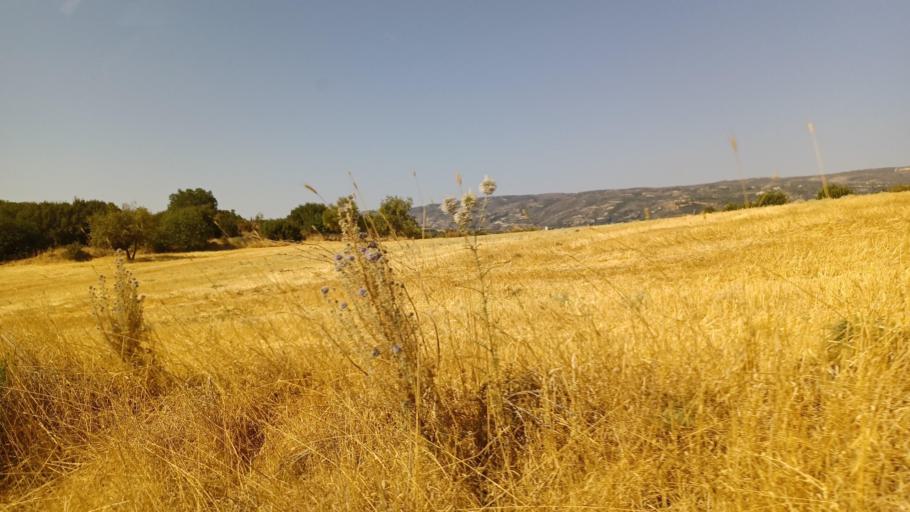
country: CY
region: Pafos
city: Polis
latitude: 34.9654
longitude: 32.4936
